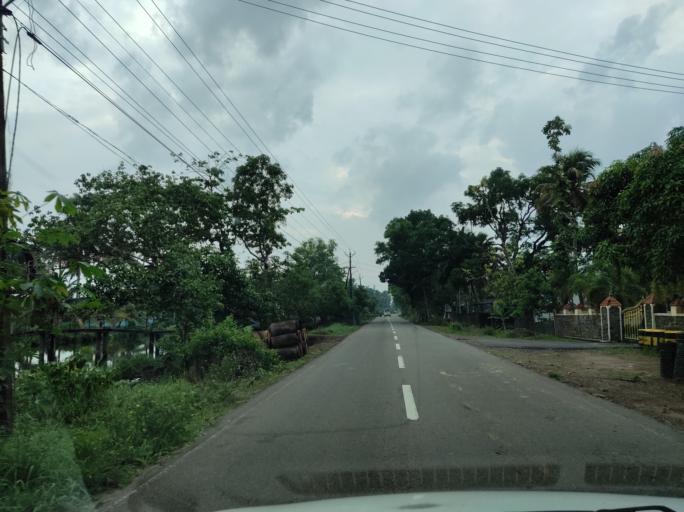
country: IN
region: Kerala
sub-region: Alappuzha
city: Kayankulam
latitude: 9.2576
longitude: 76.4196
